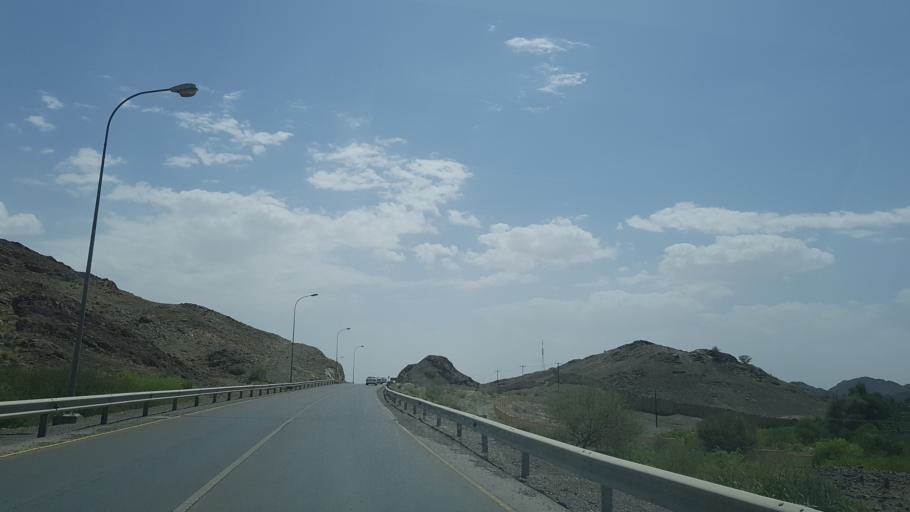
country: OM
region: Muhafazat ad Dakhiliyah
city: Bahla'
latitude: 22.9736
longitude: 57.3032
